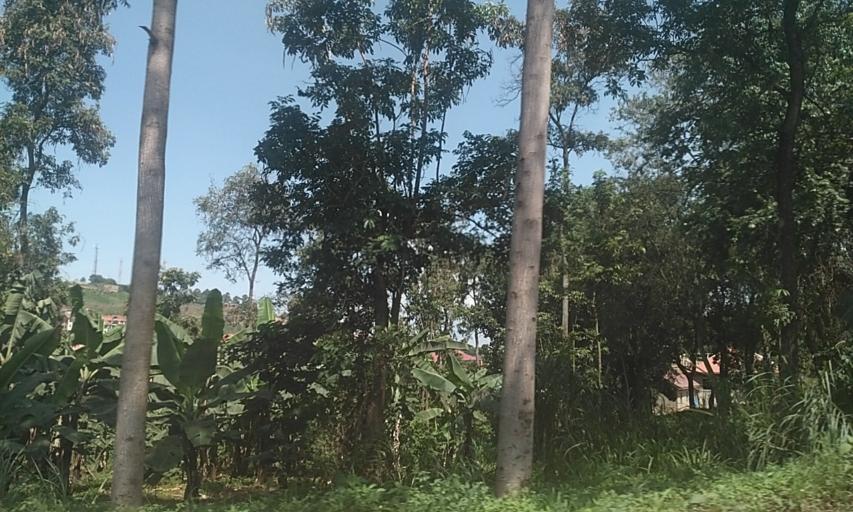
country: UG
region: Central Region
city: Kampala Central Division
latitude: 0.3859
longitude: 32.5932
